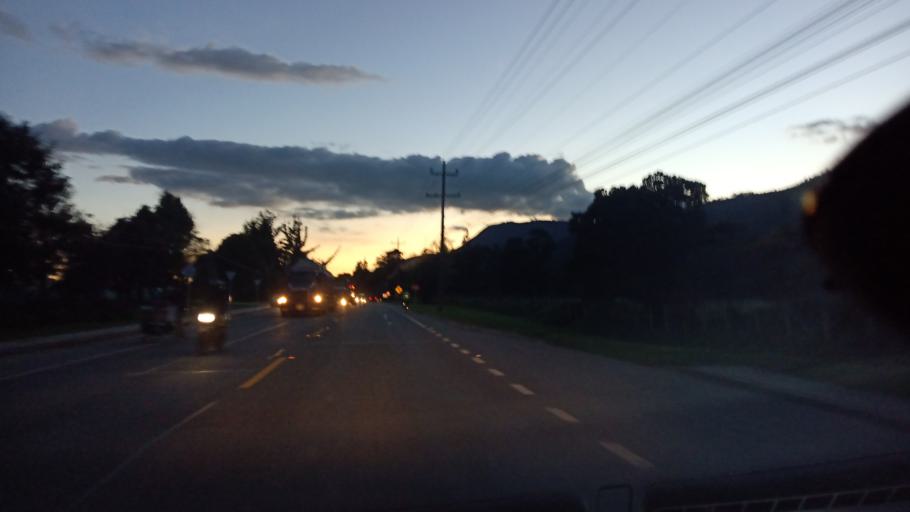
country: CO
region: Cundinamarca
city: Chia
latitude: 4.8403
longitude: -74.0840
